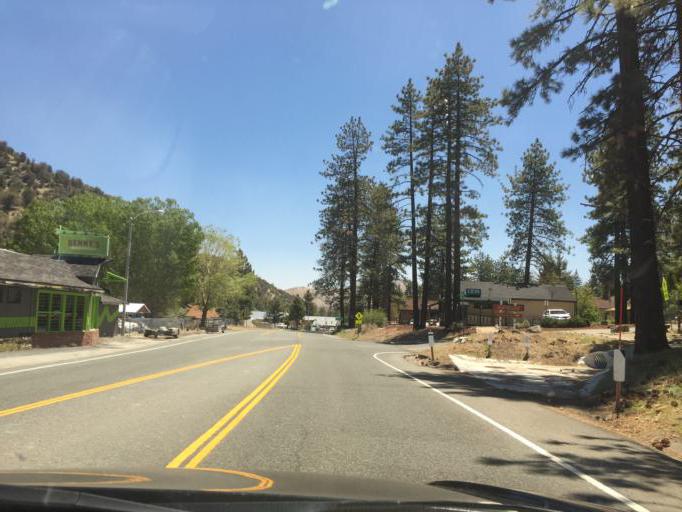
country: US
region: California
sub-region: San Bernardino County
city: Wrightwood
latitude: 34.3616
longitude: -117.6351
